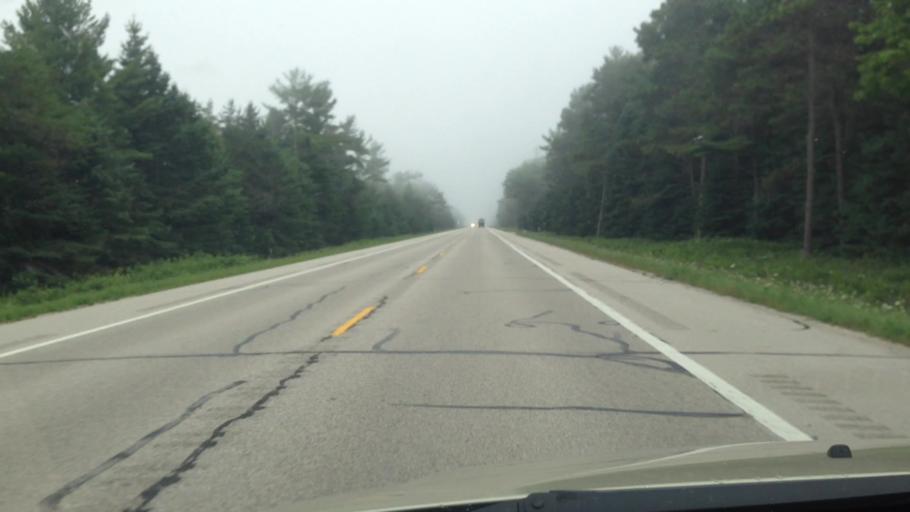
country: US
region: Michigan
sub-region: Luce County
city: Newberry
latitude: 46.0981
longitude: -85.3991
